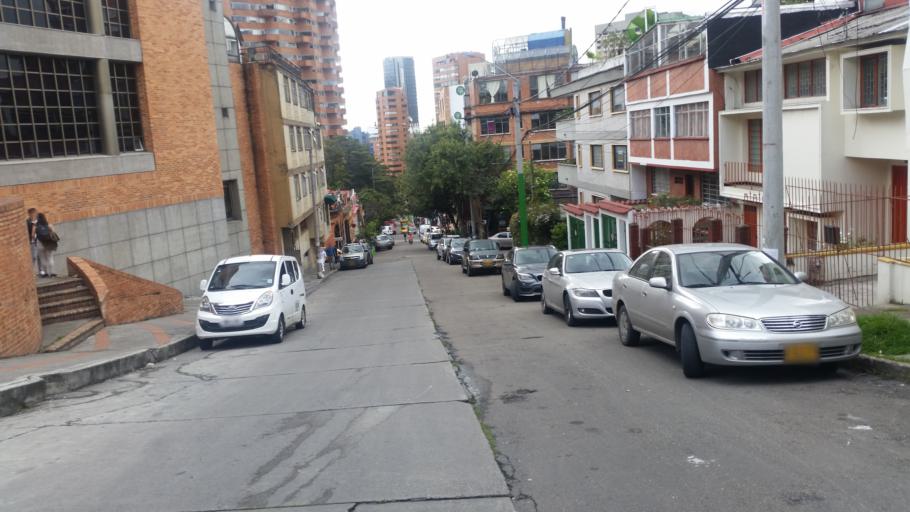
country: CO
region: Bogota D.C.
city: Bogota
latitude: 4.6140
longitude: -74.0658
